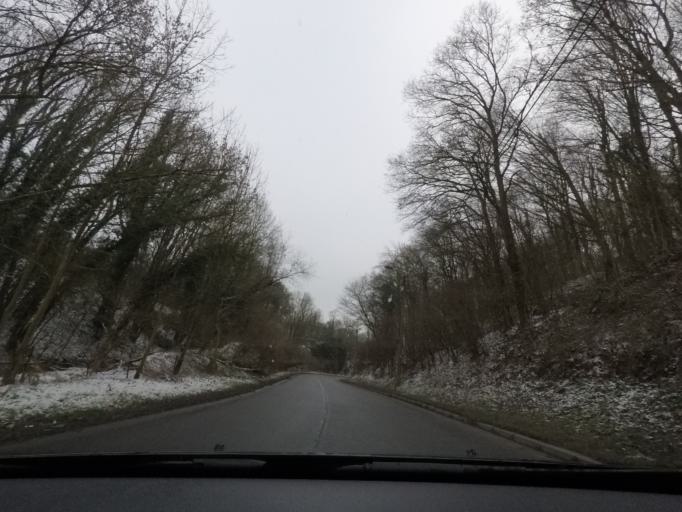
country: BE
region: Wallonia
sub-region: Province de Namur
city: Gembloux
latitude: 50.4884
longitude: 4.6866
